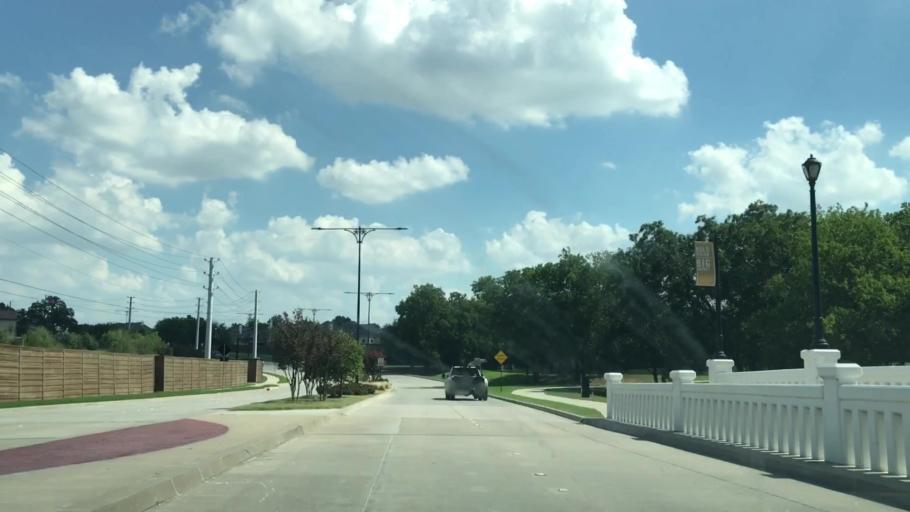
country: US
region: Texas
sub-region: Dallas County
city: Coppell
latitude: 32.9707
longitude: -97.0080
